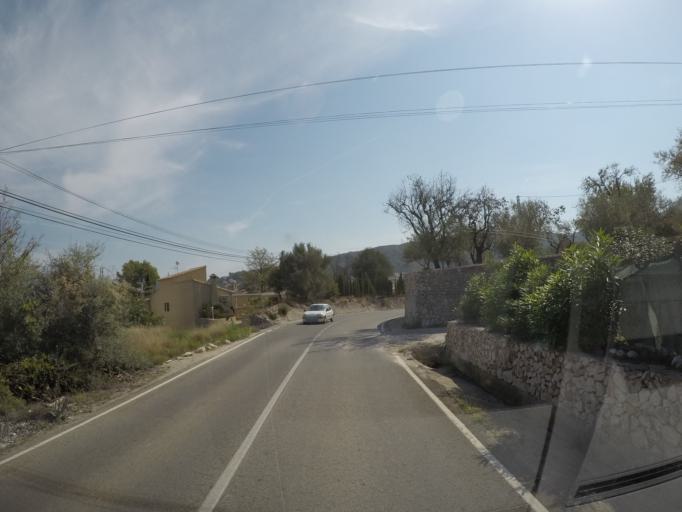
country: ES
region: Valencia
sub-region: Provincia de Alicante
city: Orba
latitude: 38.7797
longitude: -0.0684
